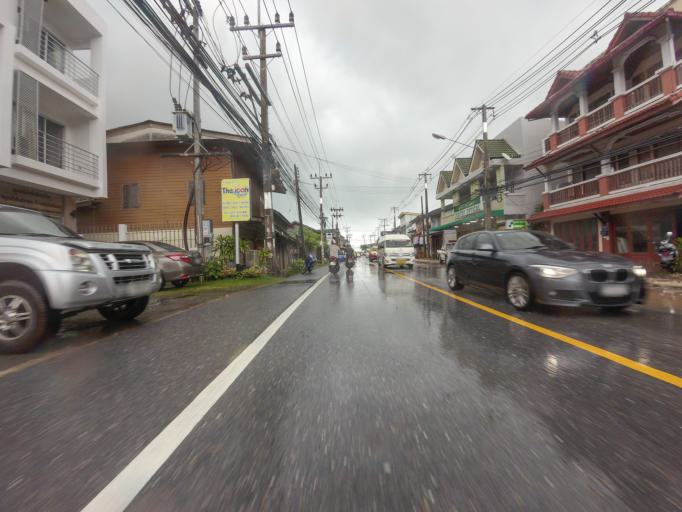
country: TH
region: Surat Thani
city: Ko Samui
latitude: 9.4433
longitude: 100.0224
